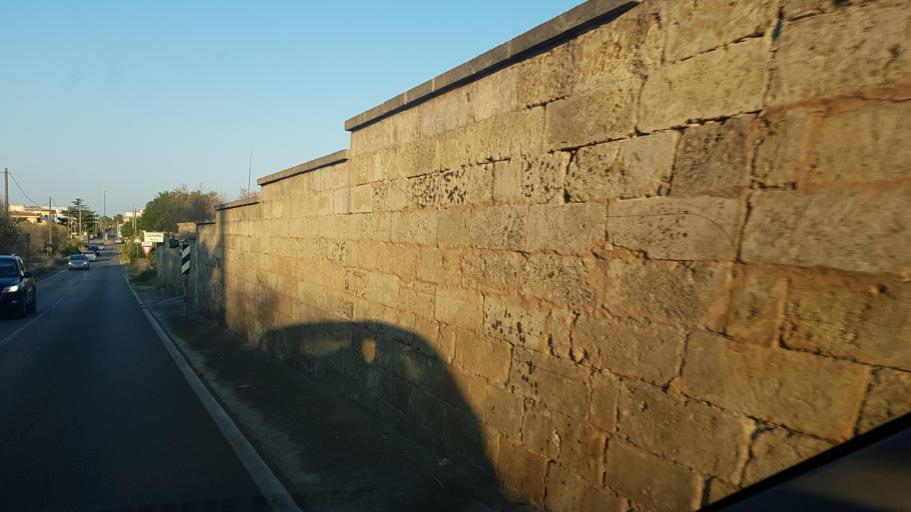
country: IT
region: Apulia
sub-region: Provincia di Lecce
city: Lucugnano
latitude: 39.9380
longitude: 18.3167
